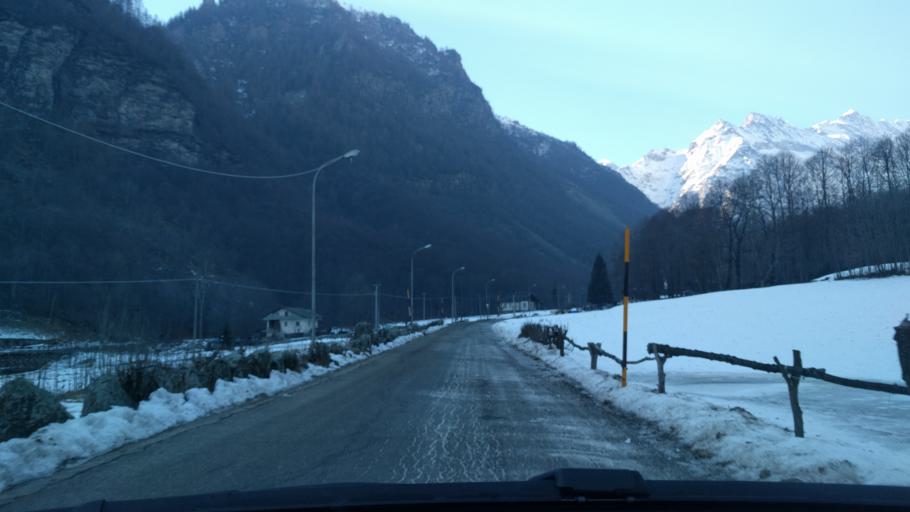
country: IT
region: Piedmont
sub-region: Provincia di Torino
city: Groscavallo
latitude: 45.3684
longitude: 7.2684
